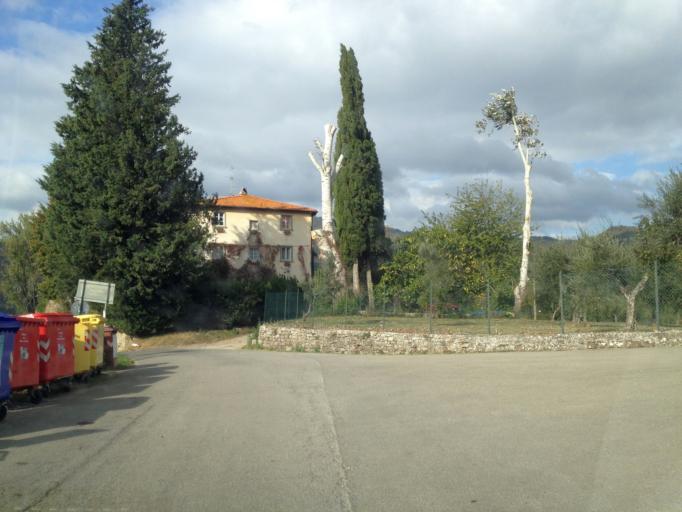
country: IT
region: Tuscany
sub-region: Province of Florence
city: Montebonello
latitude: 43.8584
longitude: 11.5046
